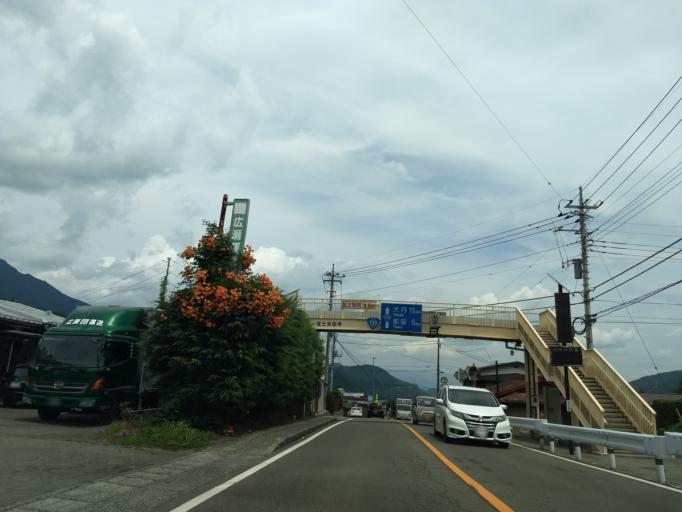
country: JP
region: Yamanashi
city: Otsuki
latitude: 35.5097
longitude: 138.8281
